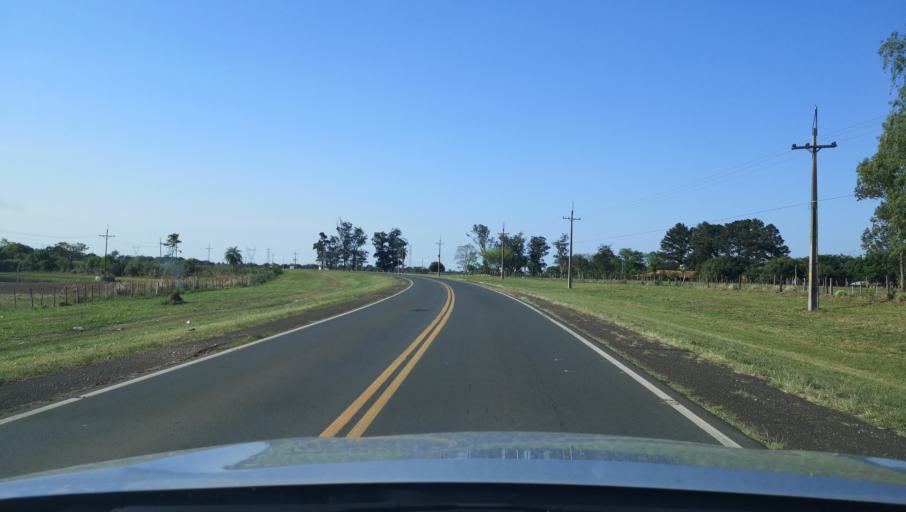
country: PY
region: Misiones
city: Santa Maria
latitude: -26.8083
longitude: -57.0204
